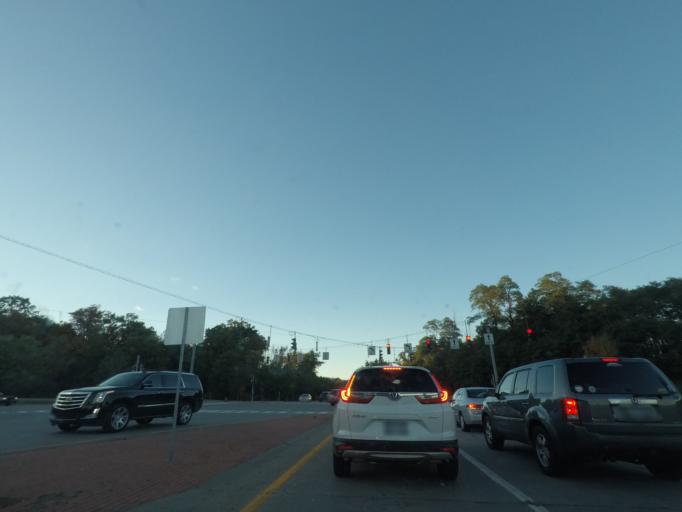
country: US
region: New York
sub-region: Albany County
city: Colonie
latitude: 42.7455
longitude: -73.8160
